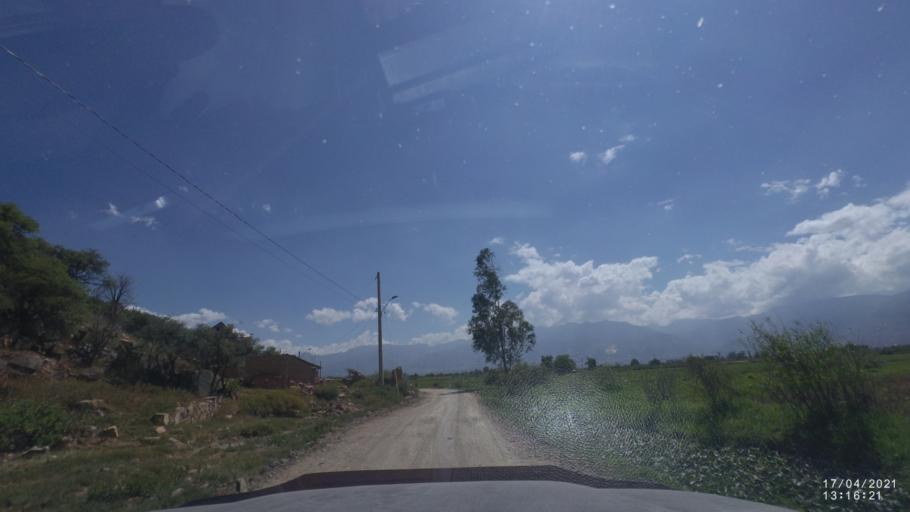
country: BO
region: Cochabamba
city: Cochabamba
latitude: -17.4169
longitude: -66.2364
